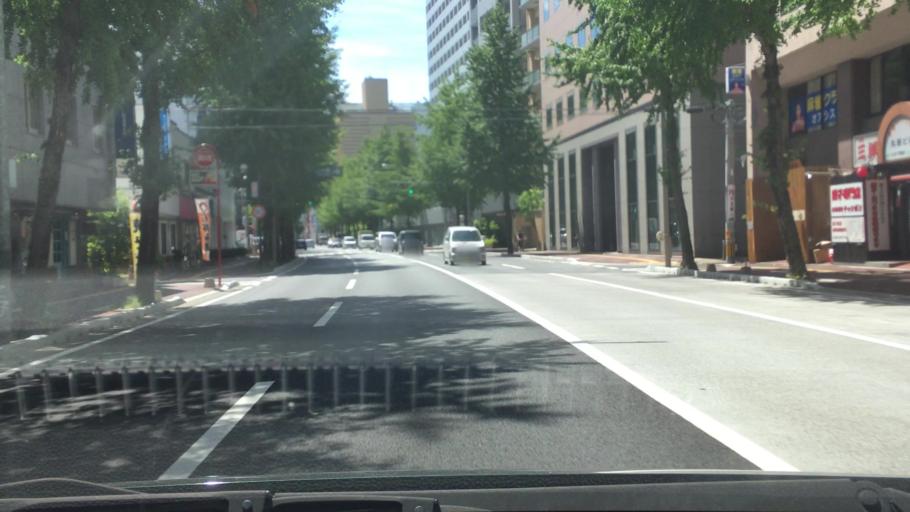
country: JP
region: Fukuoka
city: Fukuoka-shi
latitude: 33.5877
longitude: 130.4137
